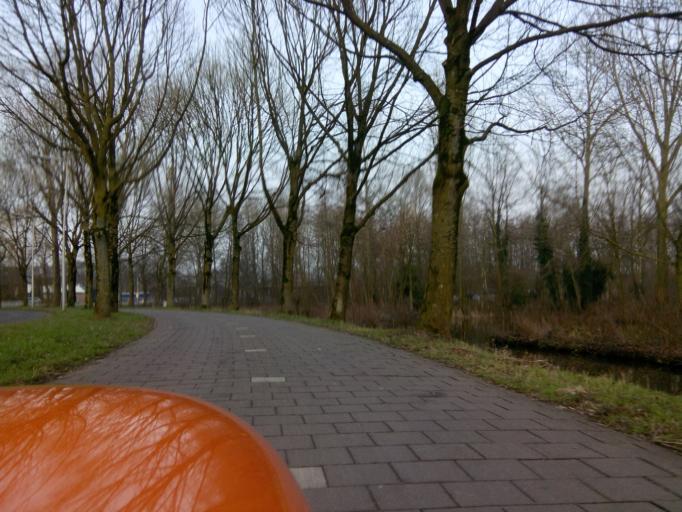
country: NL
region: Utrecht
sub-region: Gemeente De Bilt
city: De Bilt
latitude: 52.0969
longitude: 5.1543
